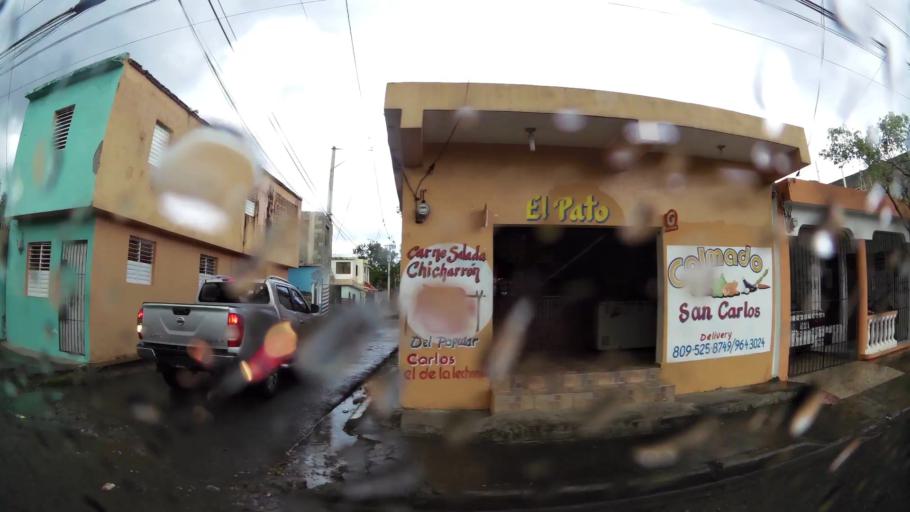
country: DO
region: Monsenor Nouel
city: Bonao
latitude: 18.9432
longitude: -70.4074
